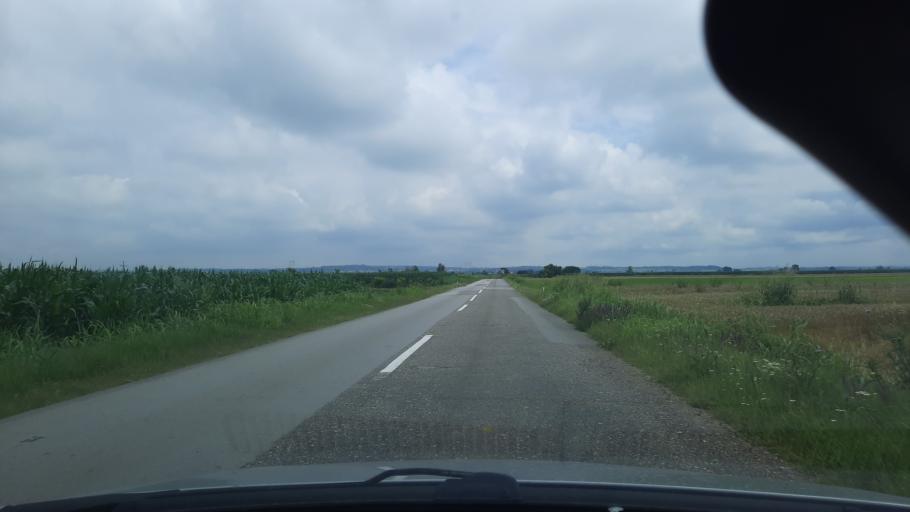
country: RS
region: Central Serbia
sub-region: Branicevski Okrug
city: Malo Crnice
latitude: 44.5813
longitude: 21.3140
